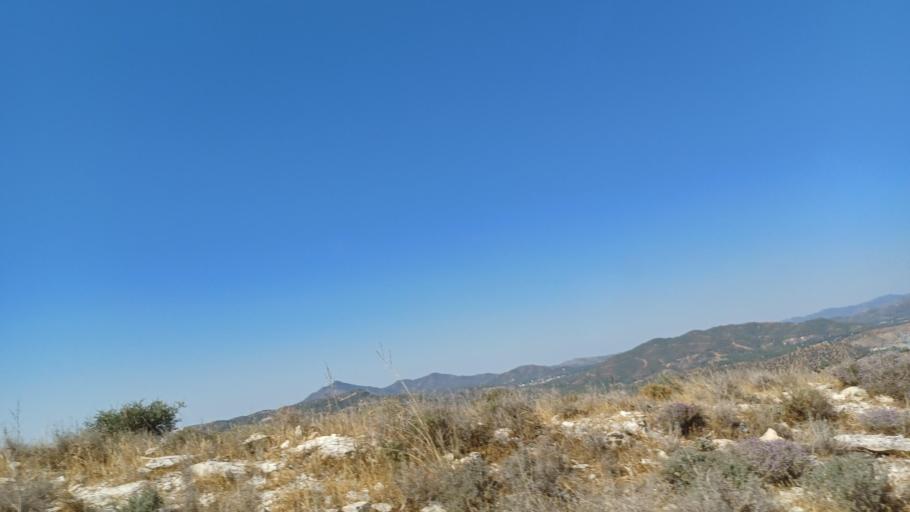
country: CY
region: Larnaka
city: Psevdas
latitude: 34.9640
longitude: 33.4791
